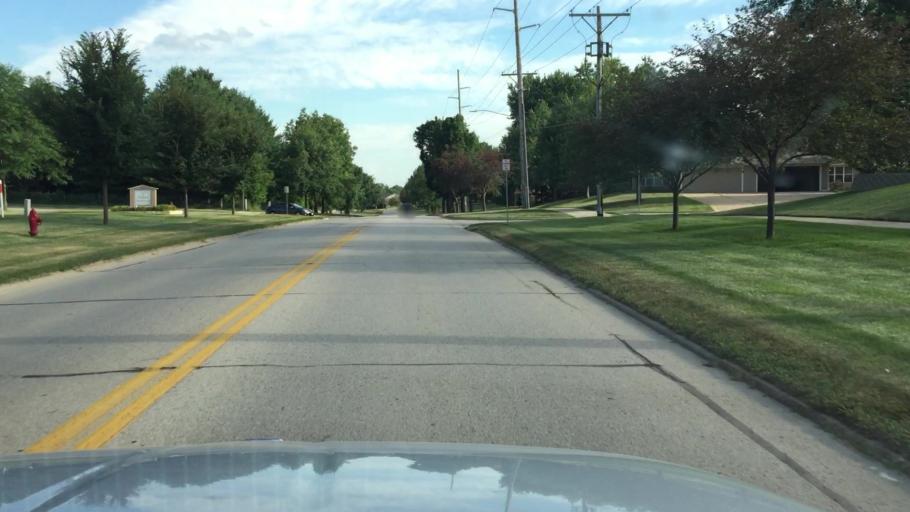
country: US
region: Iowa
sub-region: Johnson County
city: Iowa City
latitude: 41.6655
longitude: -91.4830
